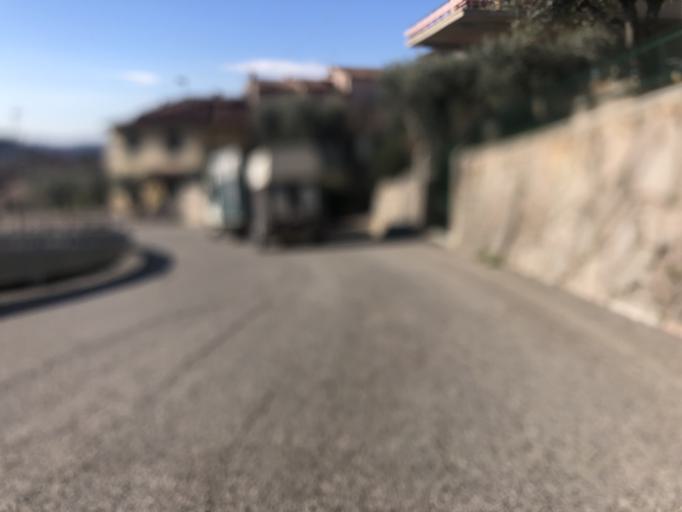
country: IT
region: Veneto
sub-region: Provincia di Verona
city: Sant'Ambrogio di Valpollicella
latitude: 45.5277
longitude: 10.8374
